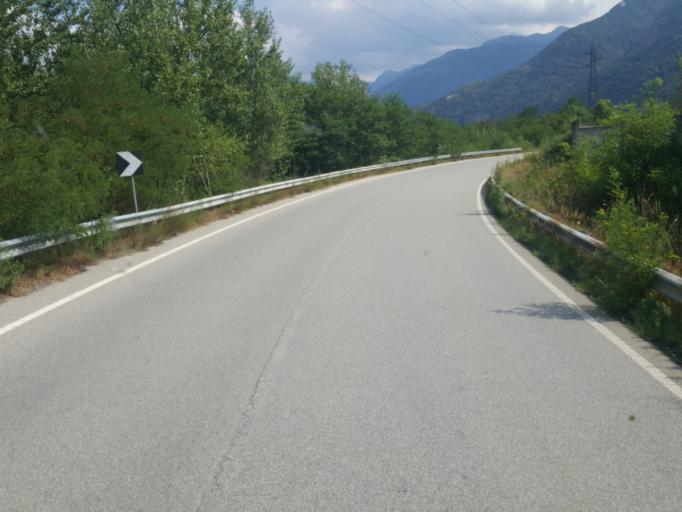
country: IT
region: Piedmont
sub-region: Provincia Verbano-Cusio-Ossola
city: Beura
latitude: 46.0791
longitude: 8.2868
